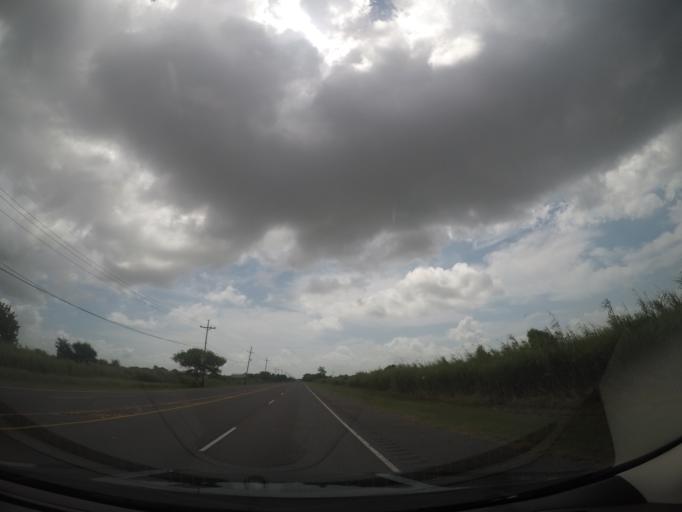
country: US
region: Louisiana
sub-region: Saint Tammany Parish
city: Eden Isle
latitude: 30.0662
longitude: -89.8239
